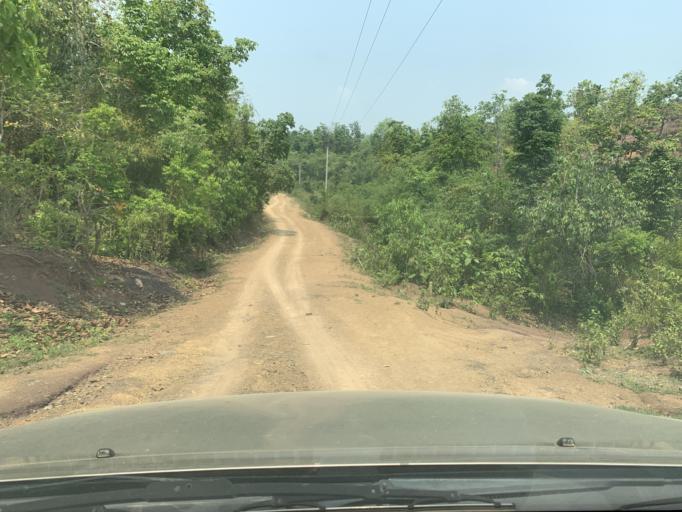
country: LA
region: Louangphabang
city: Louangphabang
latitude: 19.9494
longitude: 102.1326
